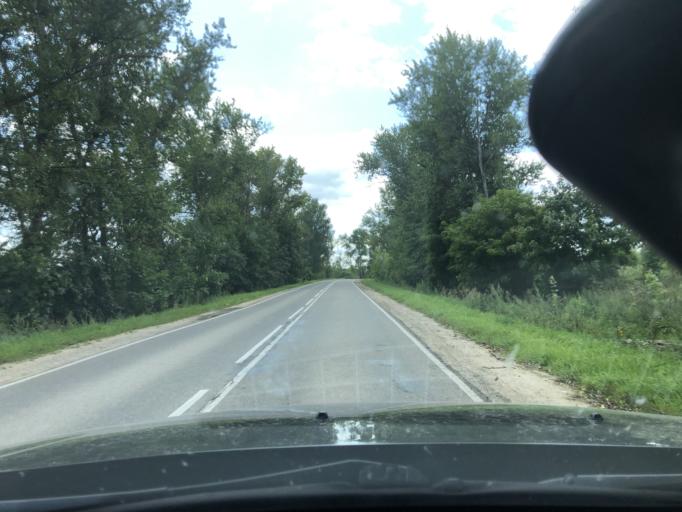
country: RU
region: Tula
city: Revyakino
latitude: 54.3561
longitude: 37.6350
